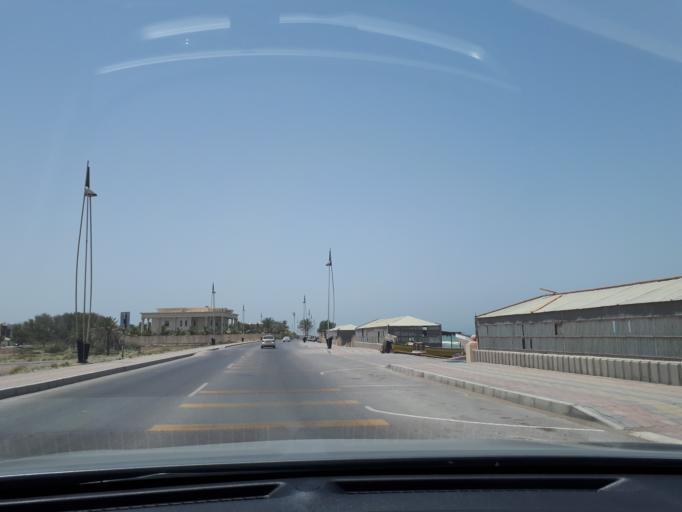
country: OM
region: Muhafazat Masqat
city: As Sib al Jadidah
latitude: 23.6662
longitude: 58.2135
